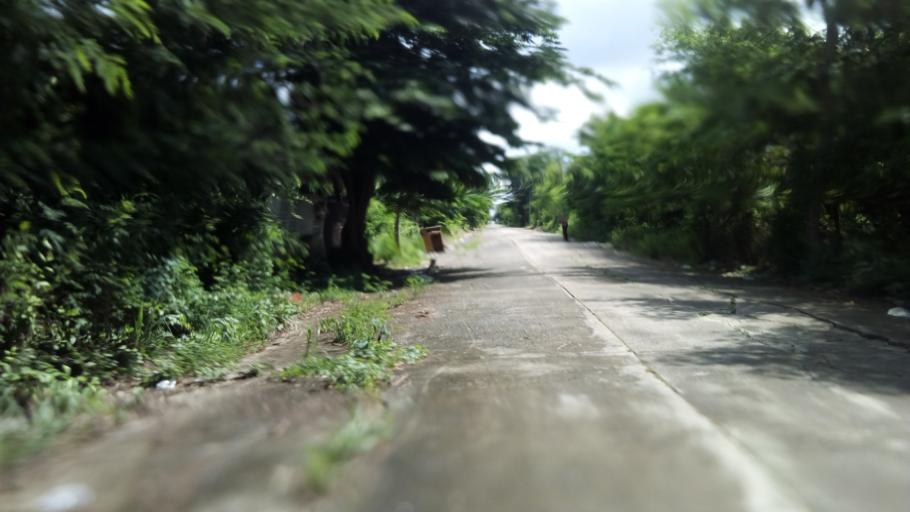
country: TH
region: Pathum Thani
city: Nong Suea
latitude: 14.0560
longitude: 100.8627
